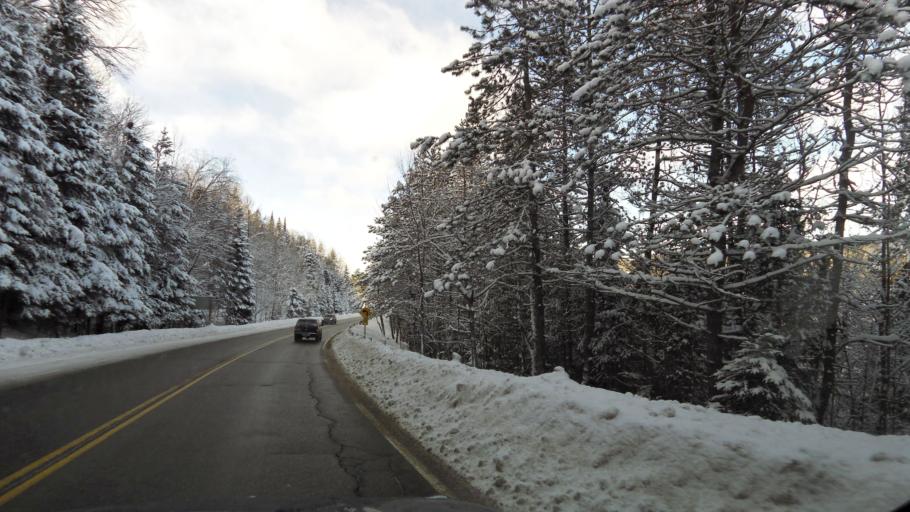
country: CA
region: Ontario
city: Bancroft
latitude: 45.0441
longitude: -78.4945
